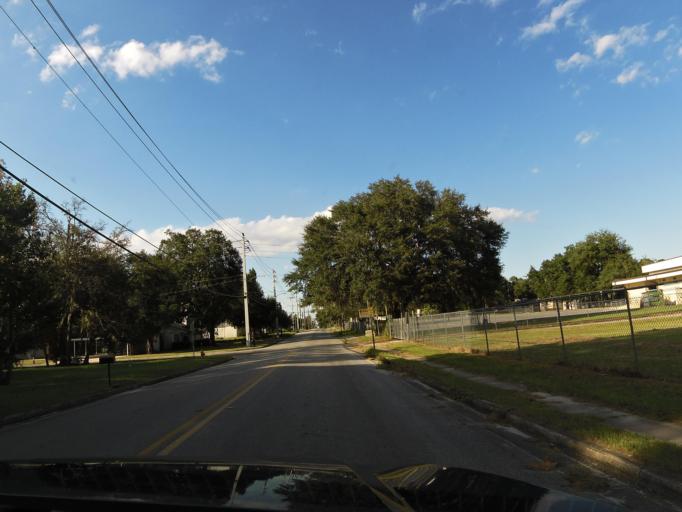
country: US
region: Florida
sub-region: Putnam County
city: Palatka
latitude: 29.6394
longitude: -81.6496
